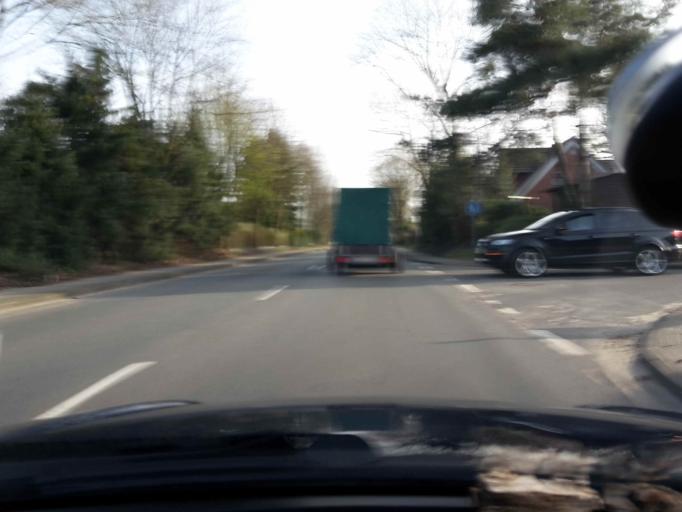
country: DE
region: Lower Saxony
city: Hollenstedt
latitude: 53.3649
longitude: 9.7116
